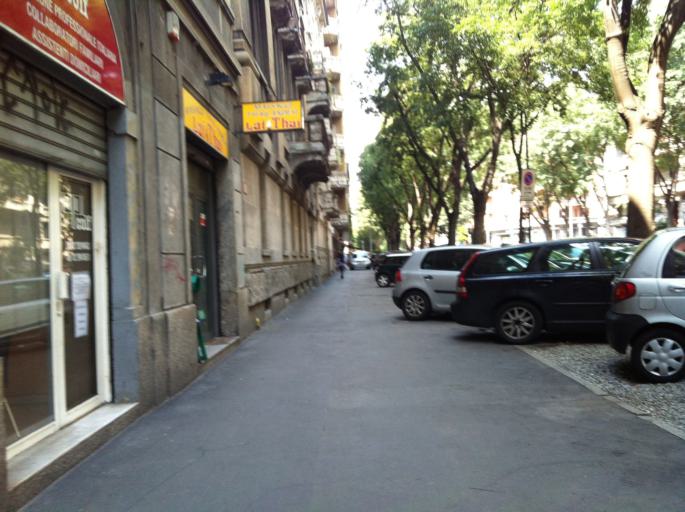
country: IT
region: Lombardy
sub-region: Citta metropolitana di Milano
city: Milano
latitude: 45.4772
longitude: 9.2150
